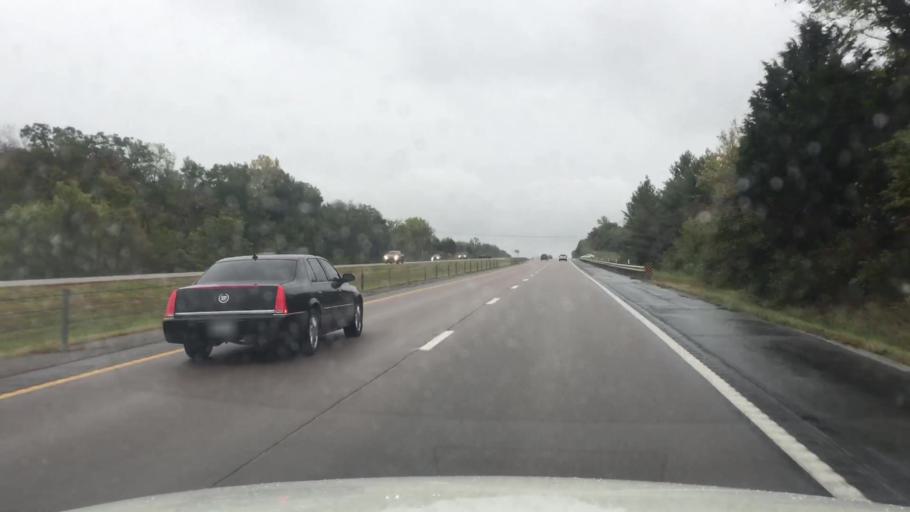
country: US
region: Missouri
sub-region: Boone County
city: Ashland
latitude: 38.7003
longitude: -92.2550
